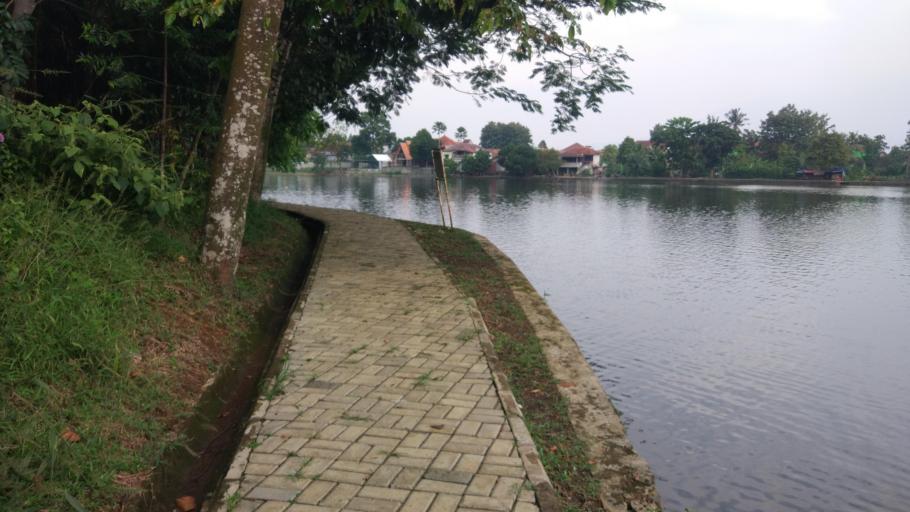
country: ID
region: West Java
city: Ciampea
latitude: -6.5517
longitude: 106.7473
